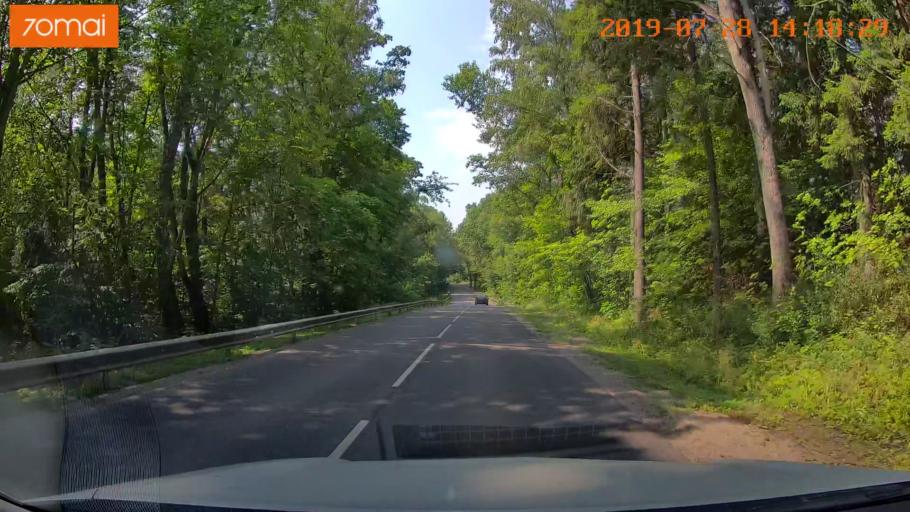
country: RU
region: Kaliningrad
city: Volochayevskoye
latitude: 54.8174
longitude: 20.2397
